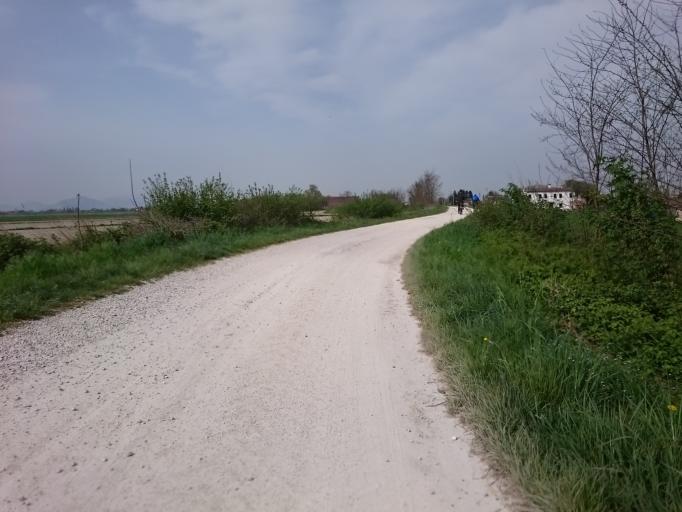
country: IT
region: Veneto
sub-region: Provincia di Padova
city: Tribano
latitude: 45.1789
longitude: 11.8427
